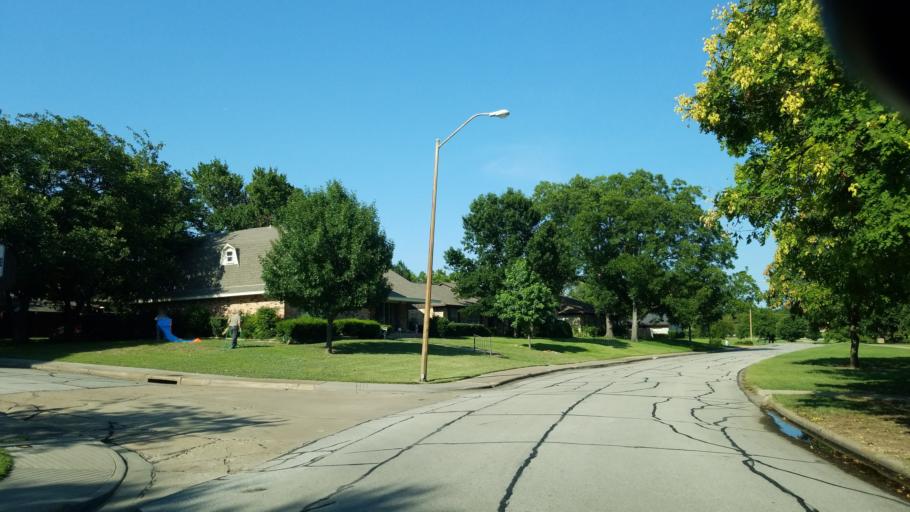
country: US
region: Texas
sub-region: Dallas County
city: Farmers Branch
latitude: 32.9269
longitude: -96.8857
